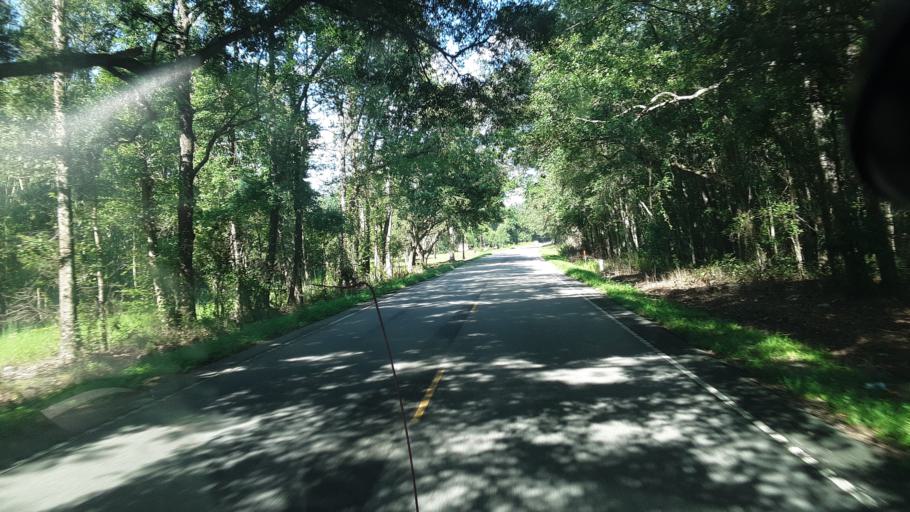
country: US
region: South Carolina
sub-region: Jasper County
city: Ridgeland
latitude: 32.5900
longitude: -80.9621
